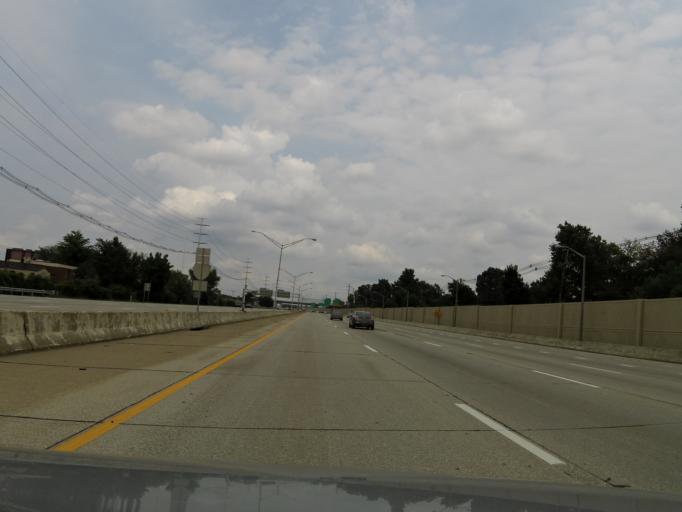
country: US
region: Kentucky
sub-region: Jefferson County
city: Saint Regis Park
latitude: 38.2302
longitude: -85.6326
